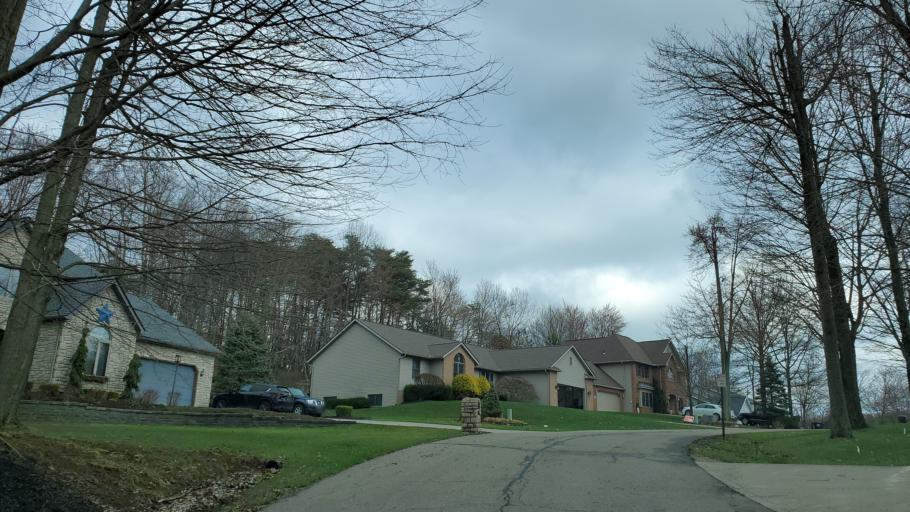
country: US
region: Ohio
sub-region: Licking County
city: Newark
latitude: 40.0344
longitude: -82.3812
